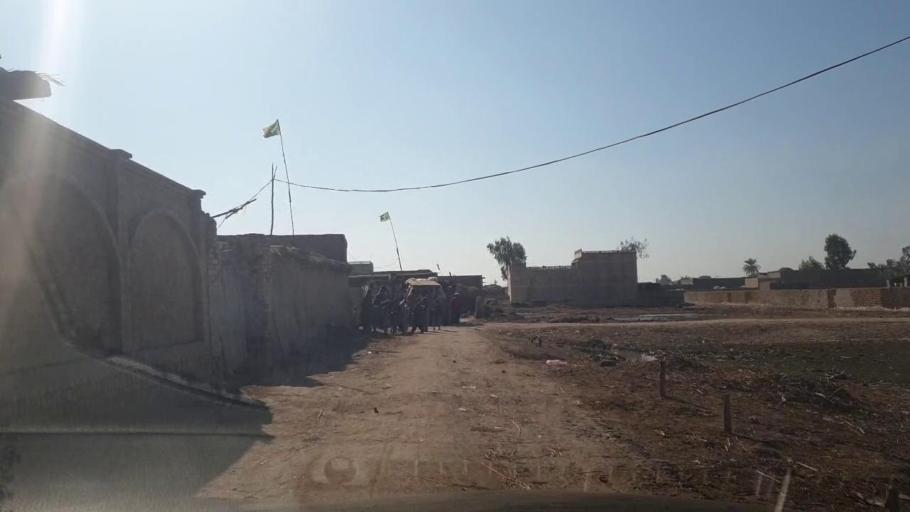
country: PK
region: Sindh
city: Ghotki
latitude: 27.9990
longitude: 69.3589
